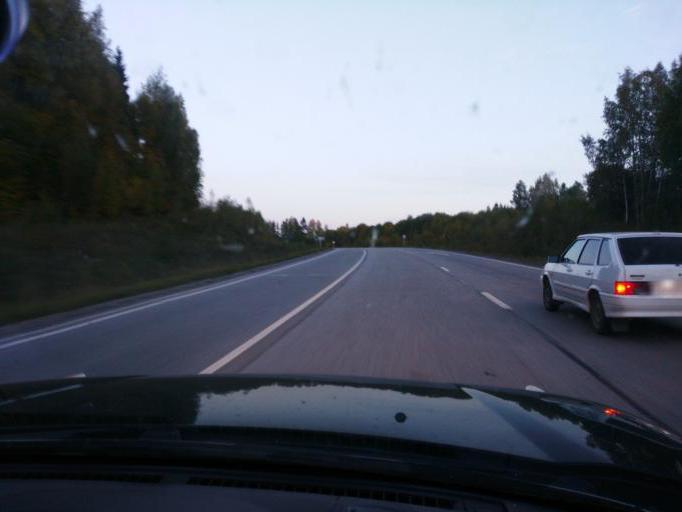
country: RU
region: Perm
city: Verkhnechusovskiye Gorodki
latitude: 58.2853
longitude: 56.8979
